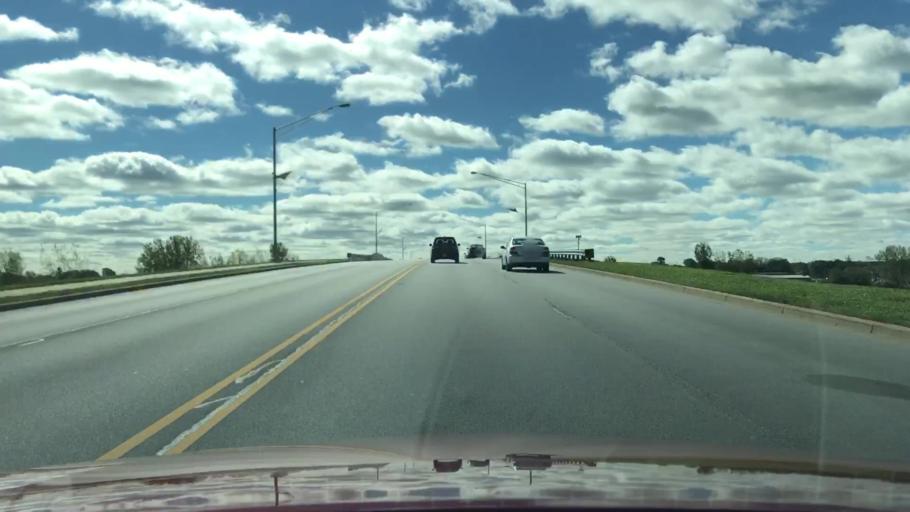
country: US
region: Indiana
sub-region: Lake County
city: Dyer
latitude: 41.5012
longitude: -87.5107
